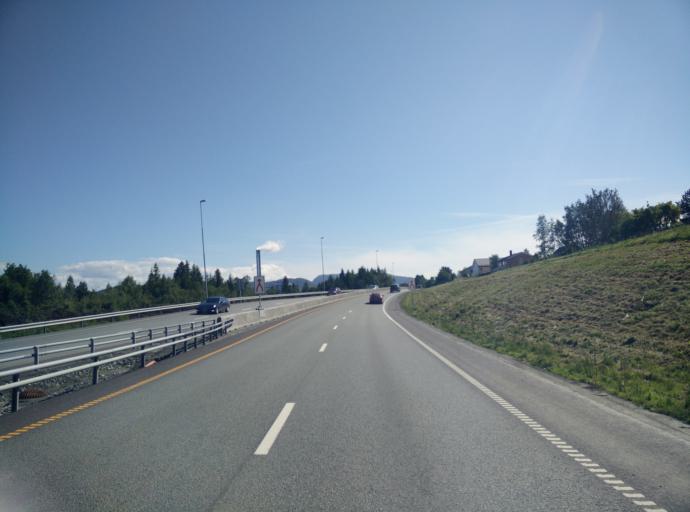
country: NO
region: Sor-Trondelag
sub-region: Trondheim
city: Trondheim
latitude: 63.3555
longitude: 10.3707
